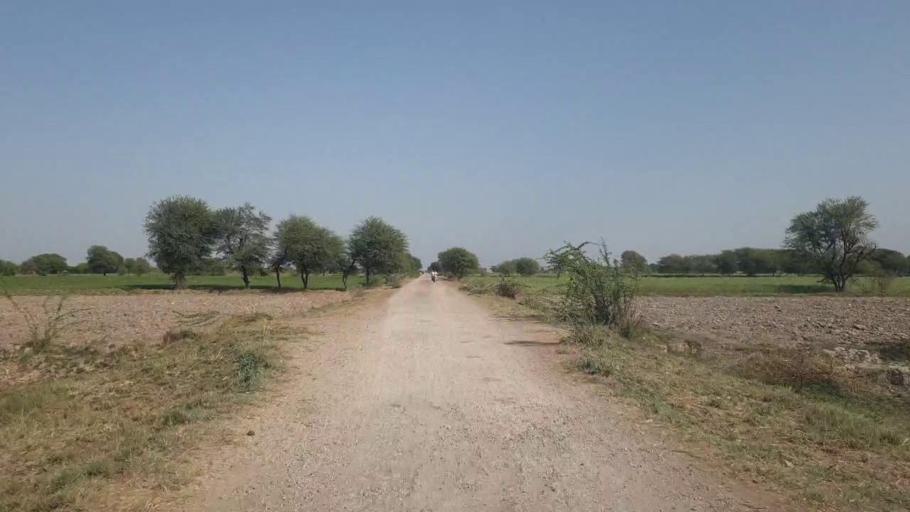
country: PK
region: Sindh
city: Dhoro Naro
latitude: 25.4421
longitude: 69.5319
